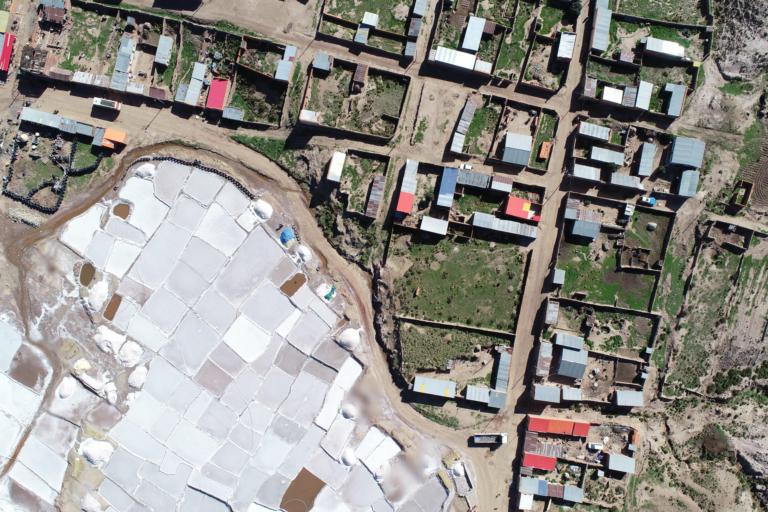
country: BO
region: La Paz
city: Patacamaya
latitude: -17.3005
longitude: -68.4829
